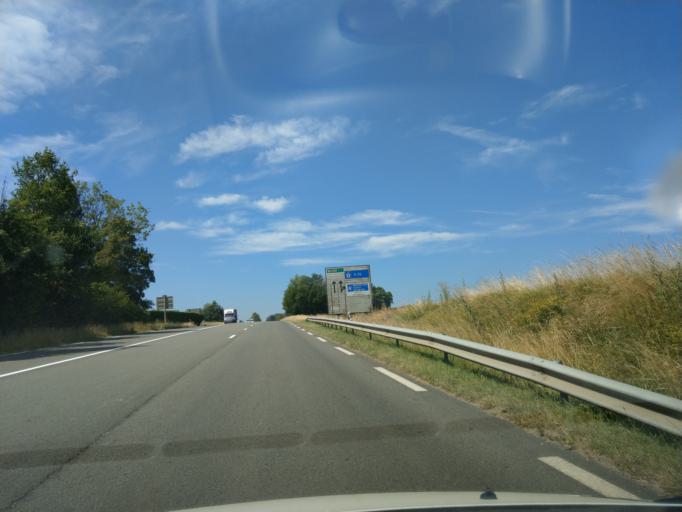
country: FR
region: Franche-Comte
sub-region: Territoire de Belfort
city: Offemont
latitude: 47.6636
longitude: 6.9103
